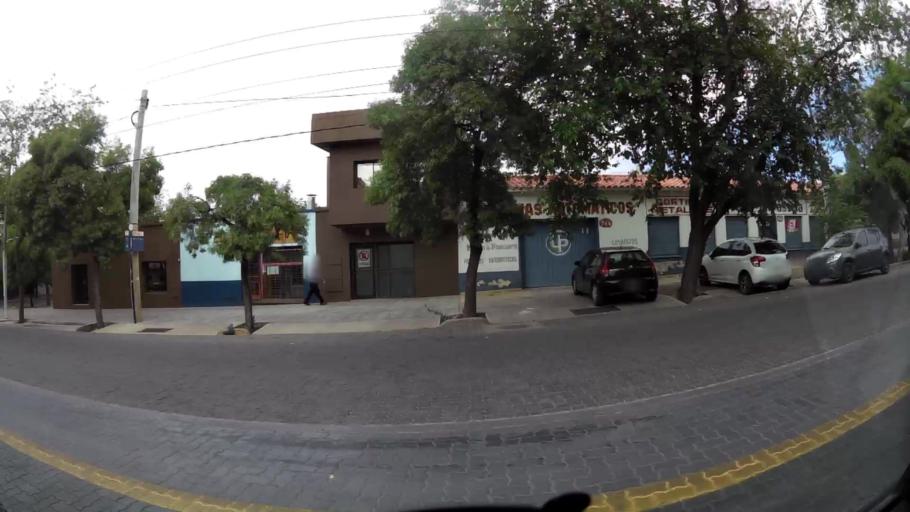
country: AR
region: Mendoza
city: Mendoza
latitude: -32.8836
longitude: -68.8591
